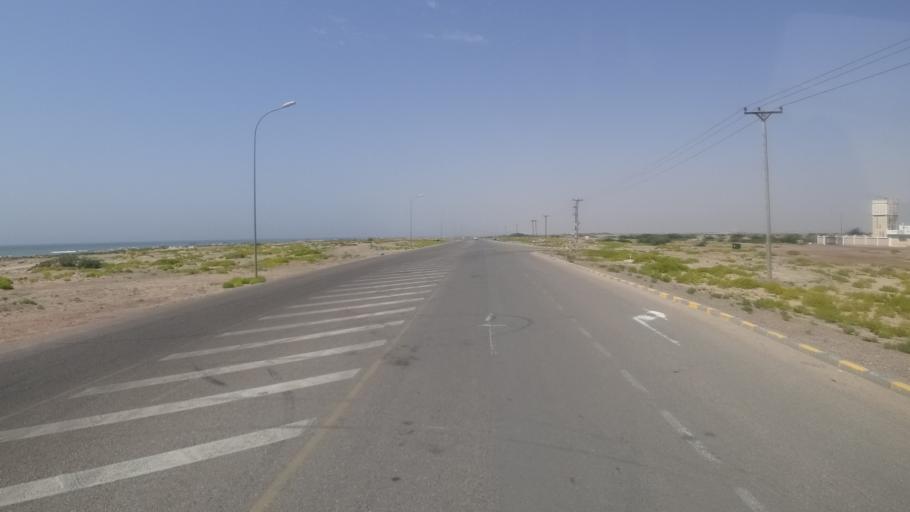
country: OM
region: Ash Sharqiyah
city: Sur
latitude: 22.1096
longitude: 59.7092
